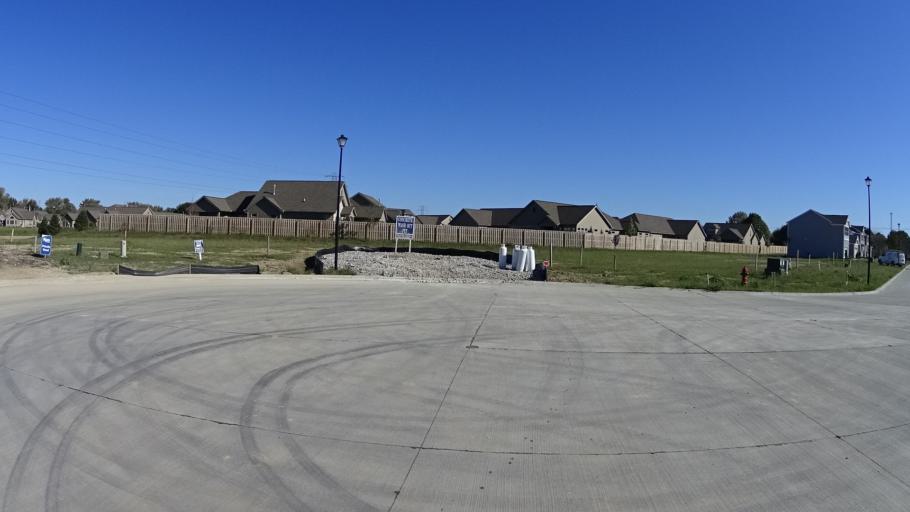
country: US
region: Ohio
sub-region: Lorain County
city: Amherst
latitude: 41.4149
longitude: -82.2214
